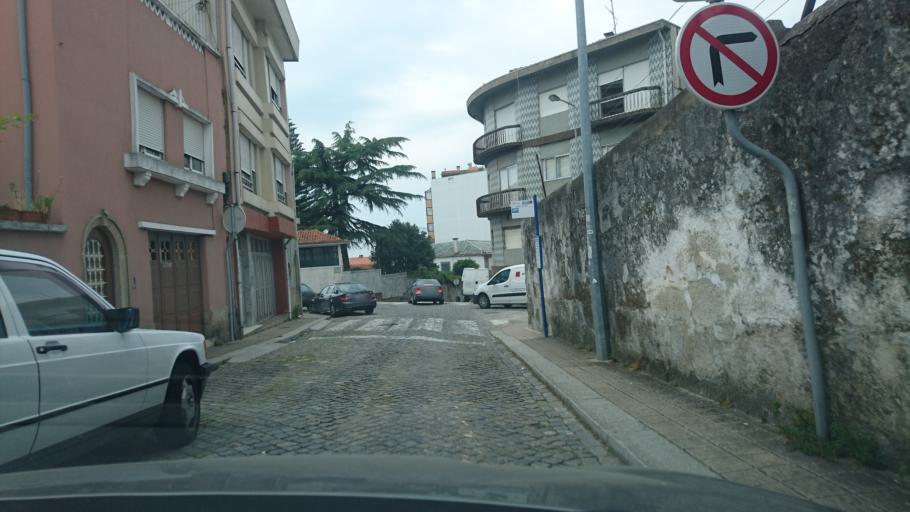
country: PT
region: Porto
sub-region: Porto
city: Porto
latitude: 41.1665
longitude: -8.6017
